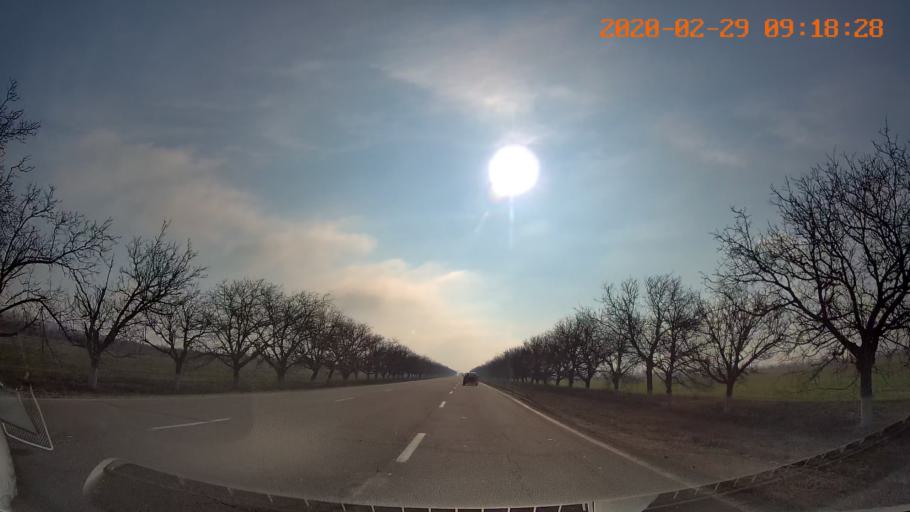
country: MD
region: Telenesti
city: Pervomaisc
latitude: 46.7733
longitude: 29.9234
